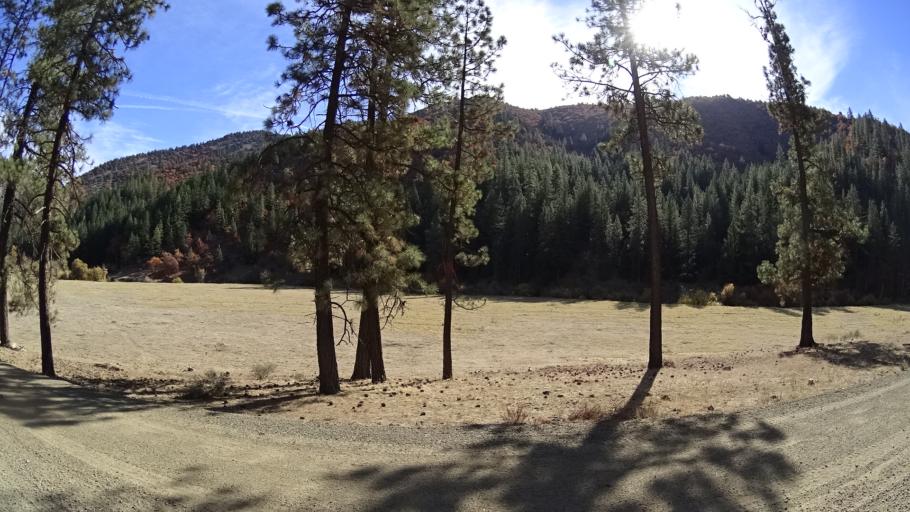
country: US
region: California
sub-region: Siskiyou County
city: Yreka
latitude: 41.6121
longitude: -122.7263
